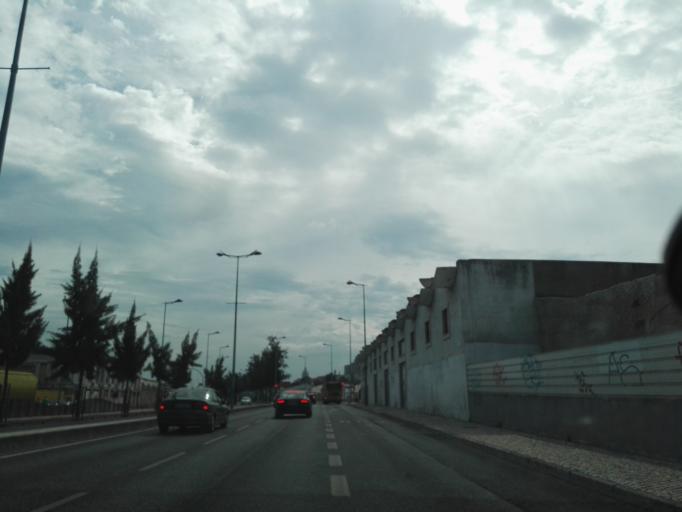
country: PT
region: Lisbon
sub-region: Lisbon
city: Lisbon
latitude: 38.7274
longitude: -9.1092
